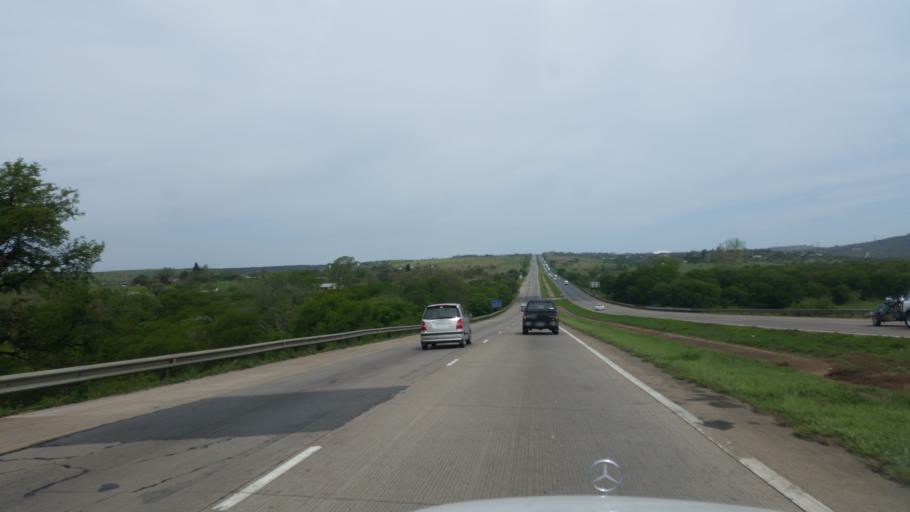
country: ZA
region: KwaZulu-Natal
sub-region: uMgungundlovu District Municipality
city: Pietermaritzburg
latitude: -29.6666
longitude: 30.4611
